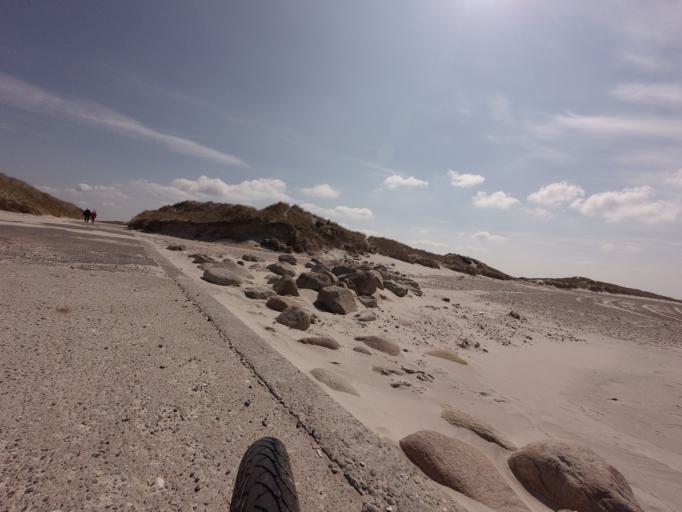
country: DK
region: North Denmark
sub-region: Jammerbugt Kommune
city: Brovst
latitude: 57.1780
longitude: 9.4367
